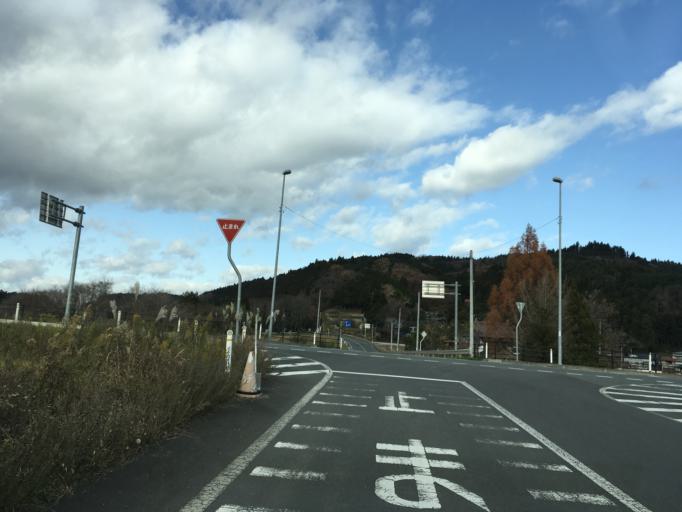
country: JP
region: Iwate
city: Ichinoseki
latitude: 38.8434
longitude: 141.2644
